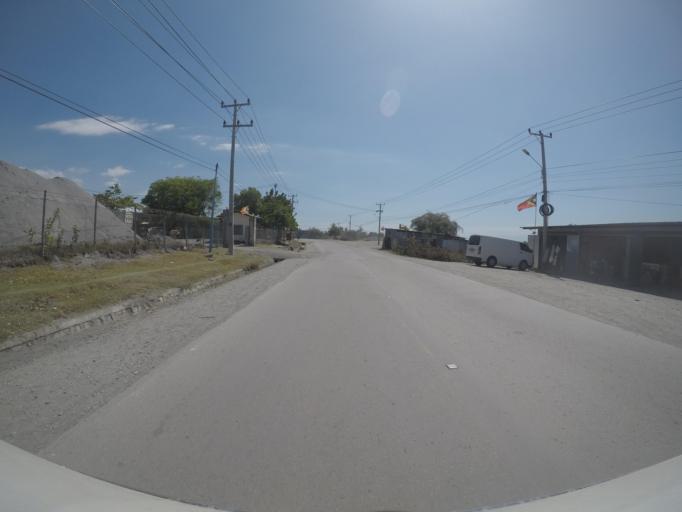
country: TL
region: Liquica
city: Liquica
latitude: -8.5901
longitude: 125.3371
